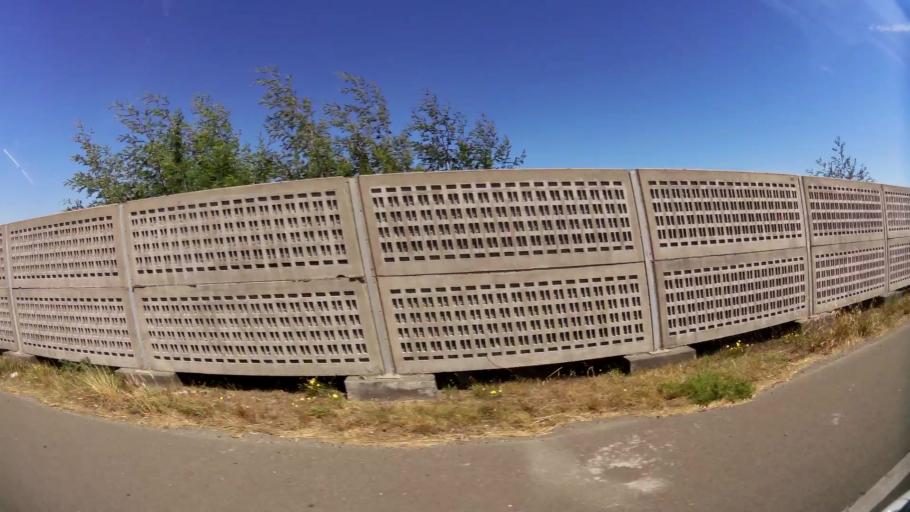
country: CL
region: Biobio
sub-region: Provincia de Concepcion
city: Talcahuano
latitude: -36.7314
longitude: -73.0958
